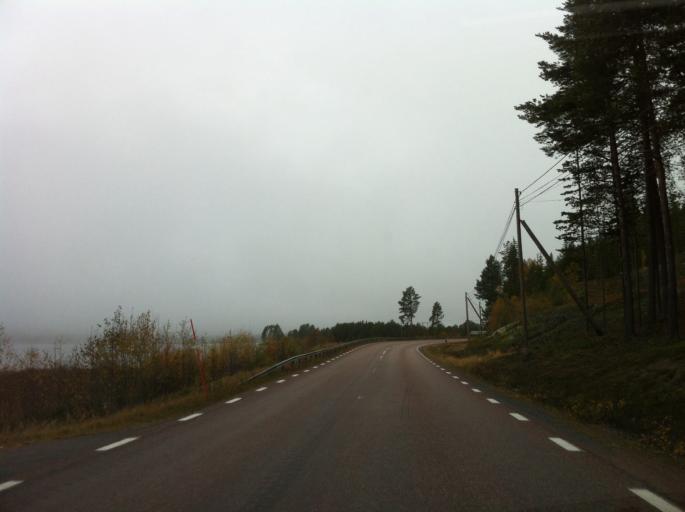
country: NO
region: Hedmark
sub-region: Trysil
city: Innbygda
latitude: 61.8536
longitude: 12.7456
